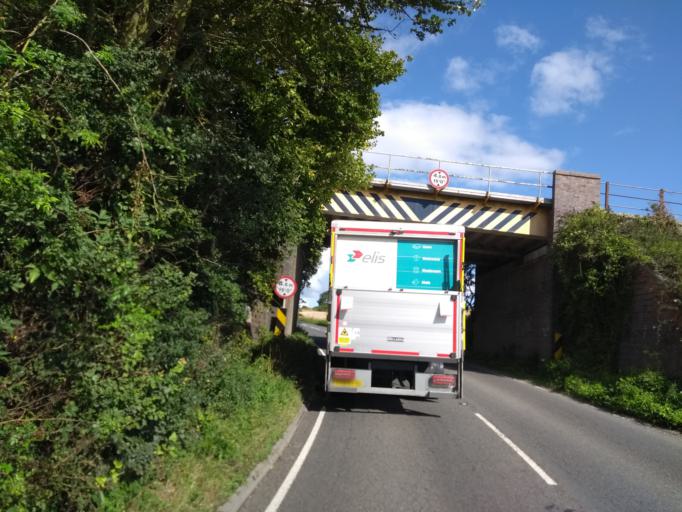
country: GB
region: England
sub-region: Somerset
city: Street
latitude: 51.0607
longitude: -2.7235
